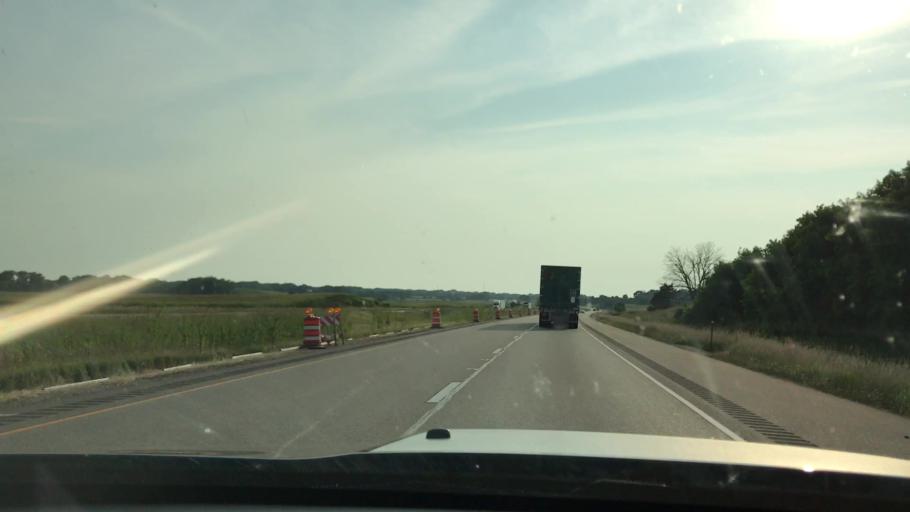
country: US
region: Illinois
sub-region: Bureau County
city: Walnut
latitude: 41.3917
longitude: -89.6516
